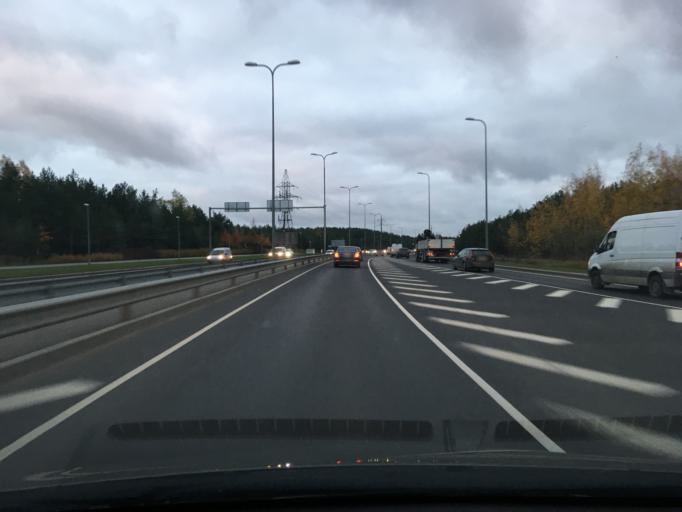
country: EE
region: Harju
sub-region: Tallinna linn
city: Tallinn
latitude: 59.4118
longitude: 24.7577
